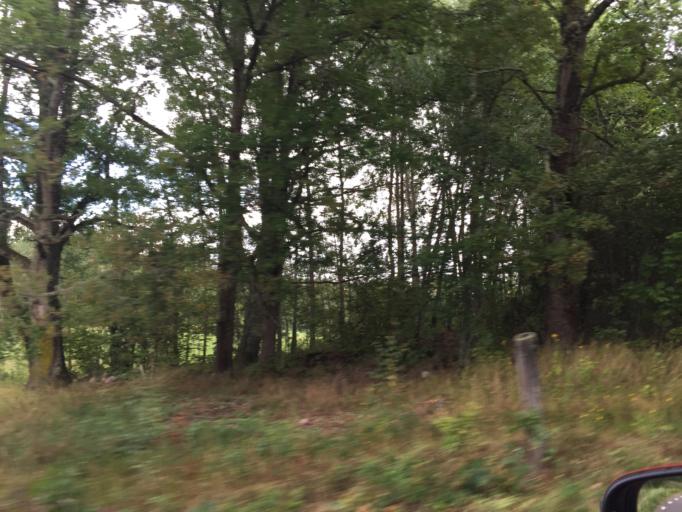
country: SE
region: Kalmar
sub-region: Vasterviks Kommun
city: Gamleby
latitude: 57.7922
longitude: 16.4505
